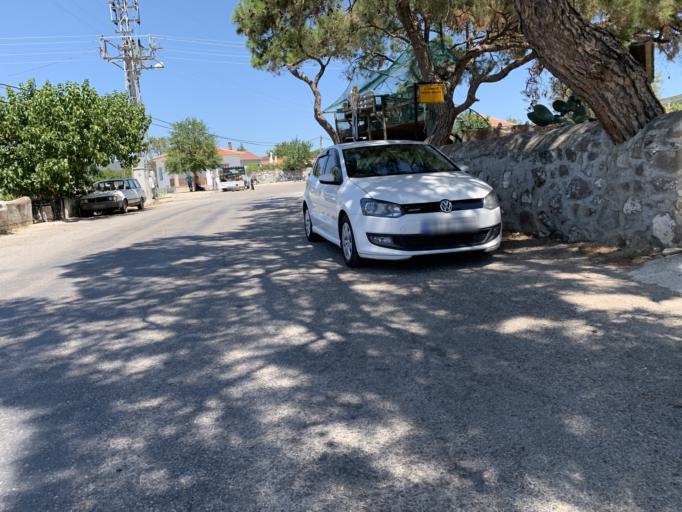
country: TR
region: Izmir
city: Uzunkuyu
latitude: 38.3220
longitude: 26.5782
